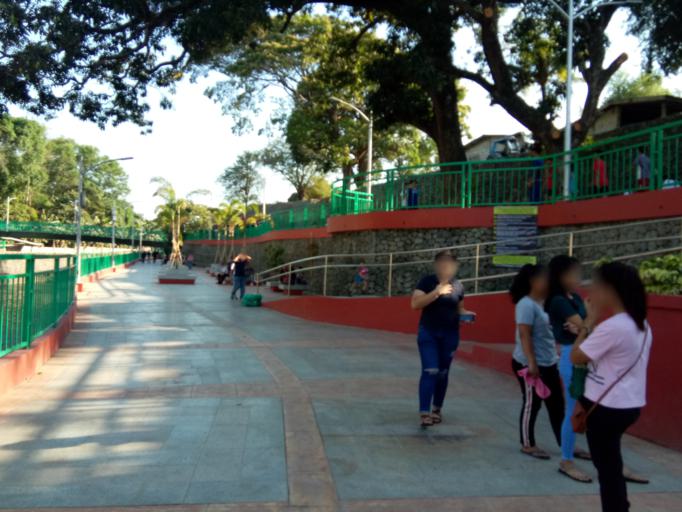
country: PH
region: Calabarzon
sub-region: Province of Cavite
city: Dasmarinas
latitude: 14.3275
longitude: 120.9559
